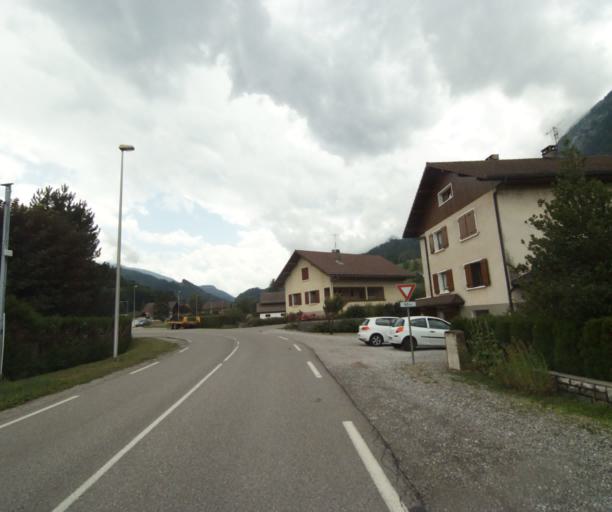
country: FR
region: Rhone-Alpes
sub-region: Departement de la Haute-Savoie
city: Thones
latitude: 45.8738
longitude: 6.3225
